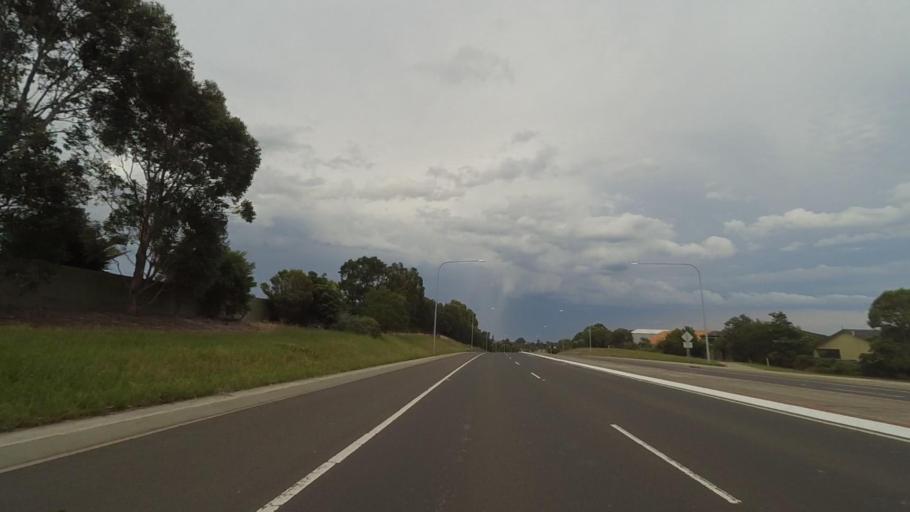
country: AU
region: New South Wales
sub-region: Shellharbour
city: Flinders
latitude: -34.5859
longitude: 150.8553
